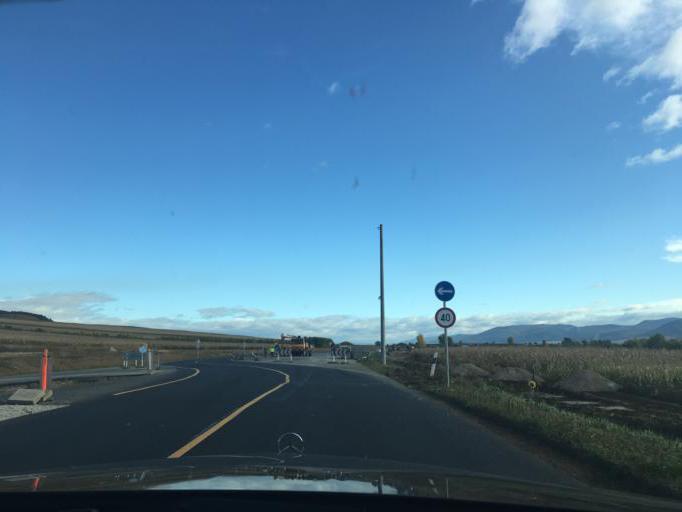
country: HU
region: Borsod-Abauj-Zemplen
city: Gonc
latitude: 48.5201
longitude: 21.2396
